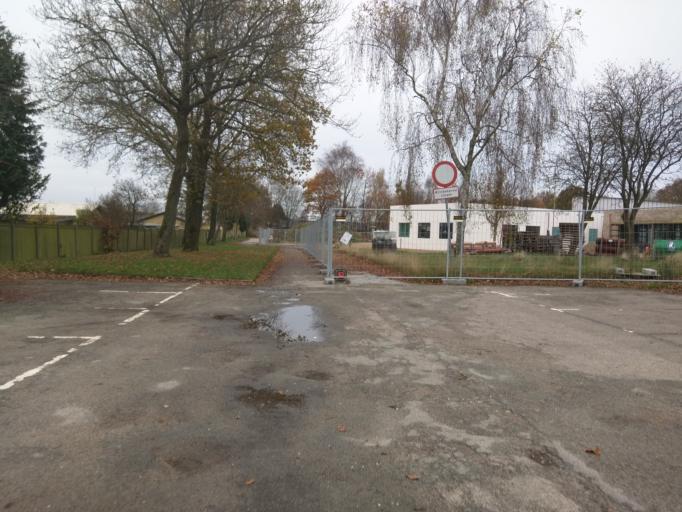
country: DK
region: Central Jutland
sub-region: Viborg Kommune
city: Viborg
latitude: 56.4633
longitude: 9.3877
